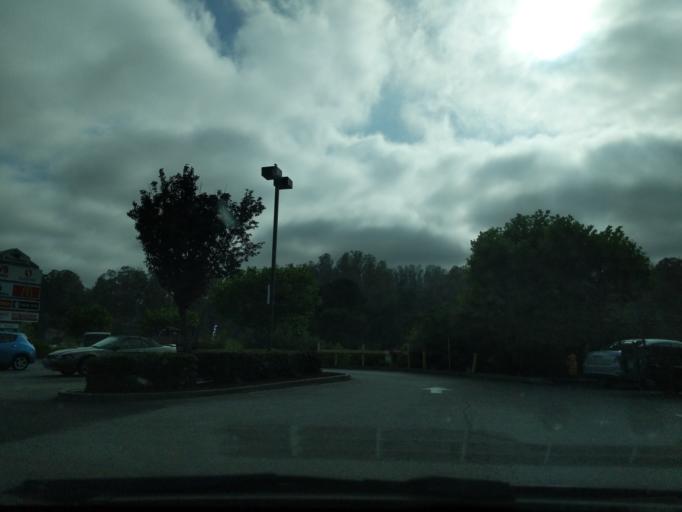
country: US
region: California
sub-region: Monterey County
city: Prunedale
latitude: 36.7933
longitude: -121.6660
